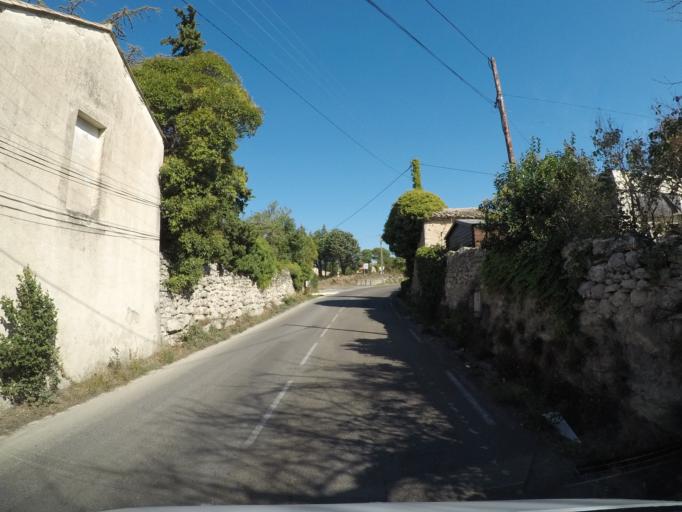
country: FR
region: Languedoc-Roussillon
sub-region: Departement du Gard
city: Uzes
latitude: 44.0095
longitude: 4.4054
